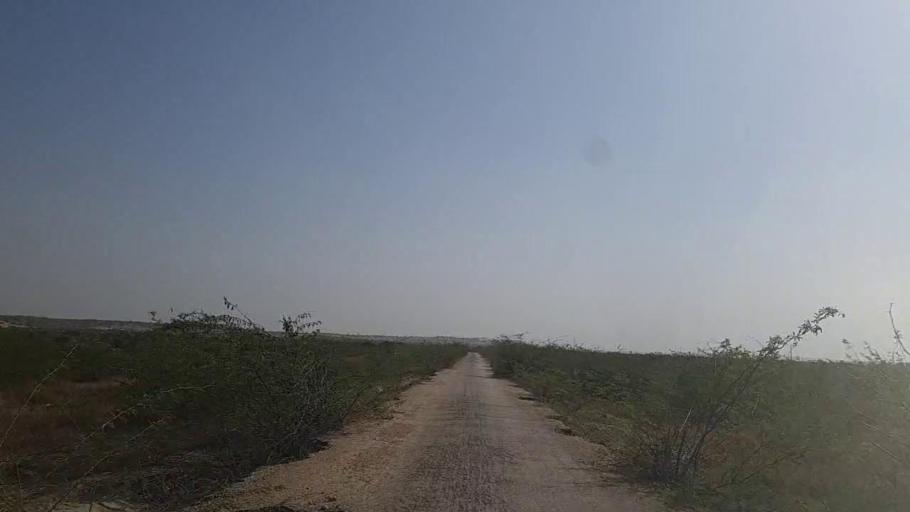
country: PK
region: Sindh
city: Naukot
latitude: 24.5909
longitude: 69.2924
